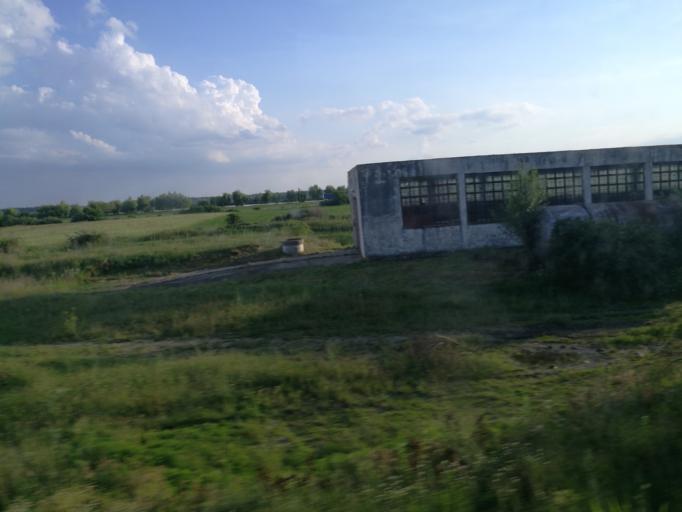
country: RO
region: Arges
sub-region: Comuna Calinesti
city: Calinesti
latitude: 44.8132
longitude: 25.0533
